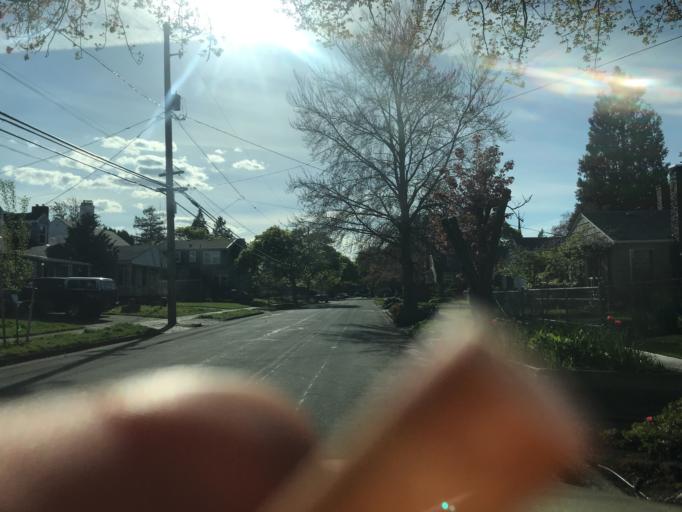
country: US
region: Oregon
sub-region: Multnomah County
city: Lents
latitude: 45.5002
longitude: -122.5874
